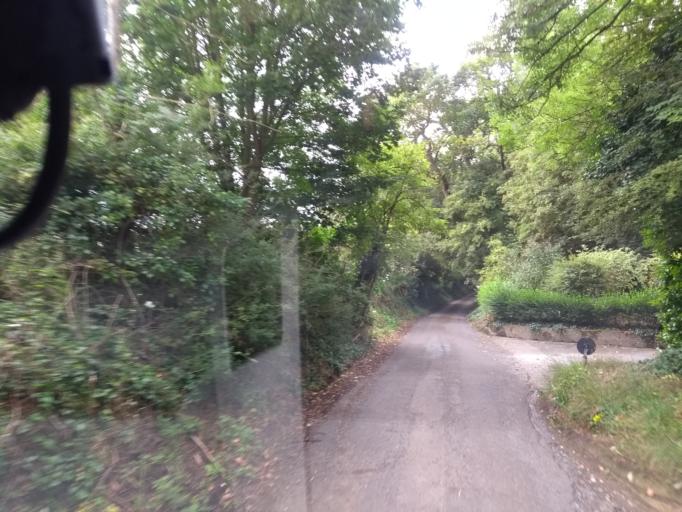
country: GB
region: England
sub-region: Somerset
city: Castle Cary
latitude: 51.0264
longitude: -2.5781
